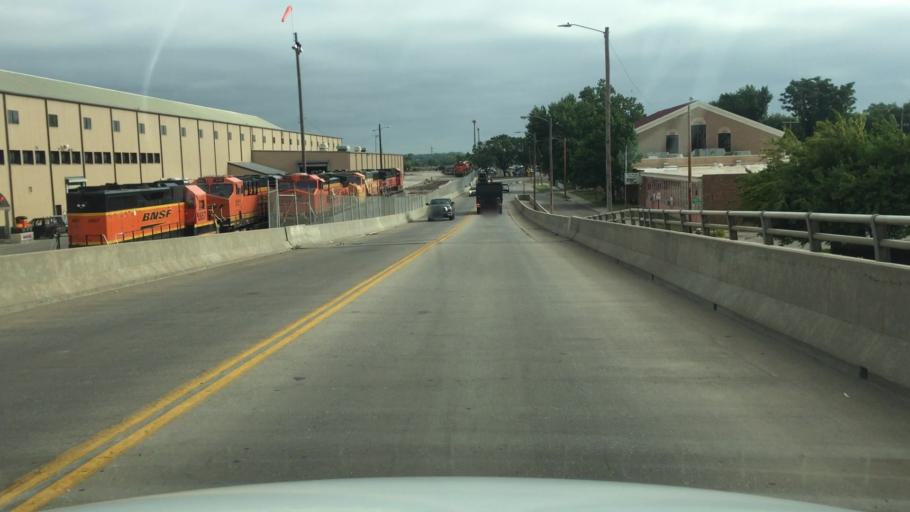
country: US
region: Kansas
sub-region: Shawnee County
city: Topeka
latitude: 39.0566
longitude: -95.6576
